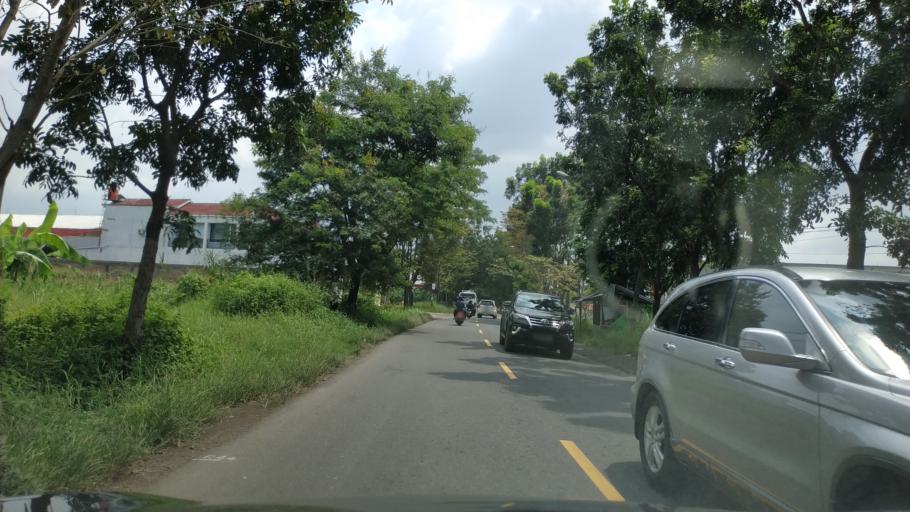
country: ID
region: Central Java
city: Lebaksiu
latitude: -7.0323
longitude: 109.1445
